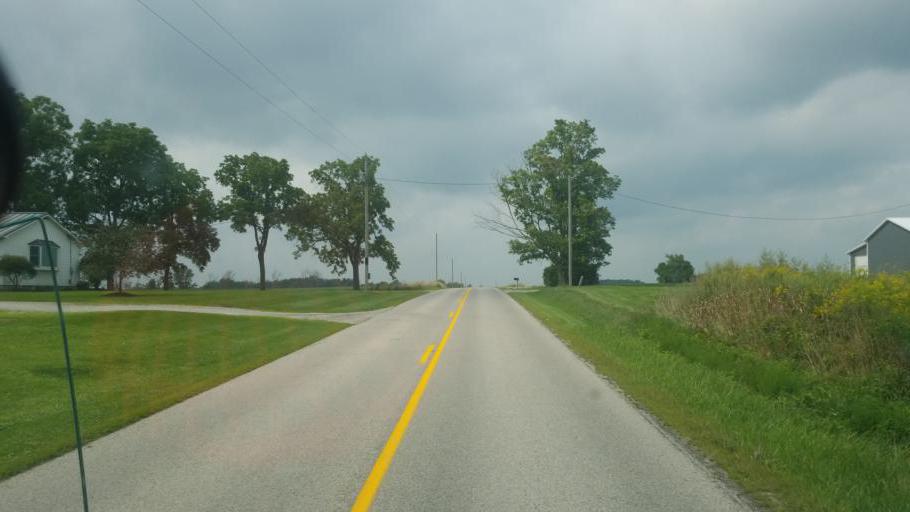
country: US
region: Ohio
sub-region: Huron County
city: Greenwich
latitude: 41.0880
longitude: -82.5717
